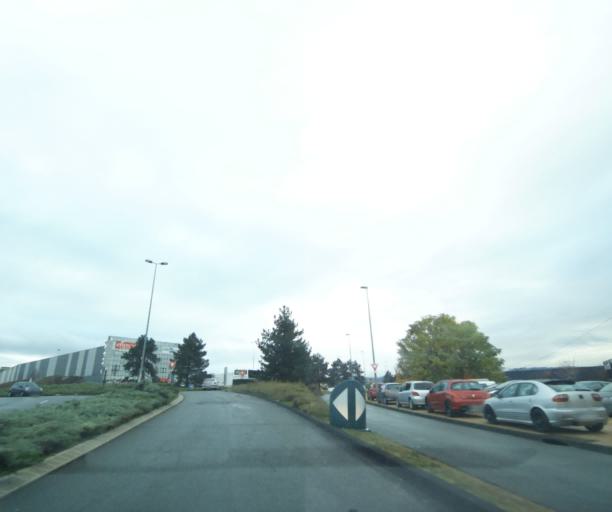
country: FR
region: Auvergne
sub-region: Departement du Puy-de-Dome
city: Aubiere
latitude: 45.7807
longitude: 3.1316
